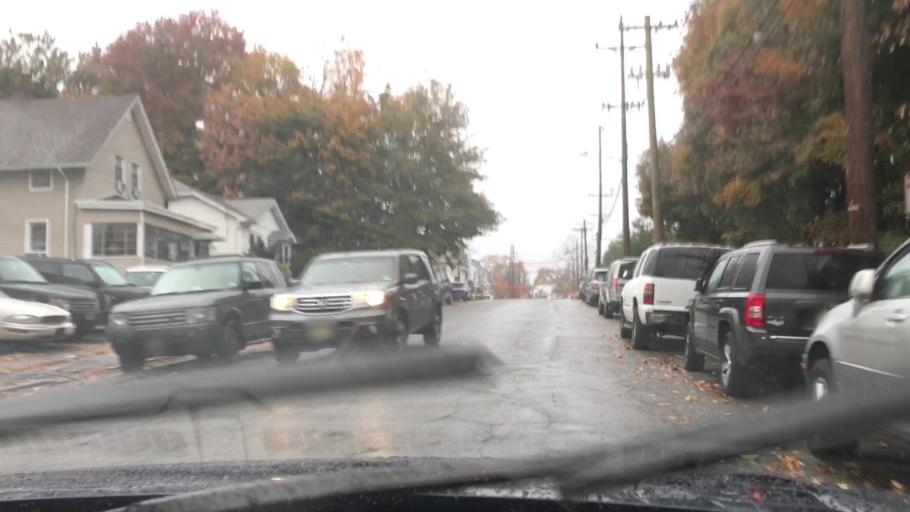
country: US
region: New Jersey
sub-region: Bergen County
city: Wallington
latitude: 40.8644
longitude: -74.1020
